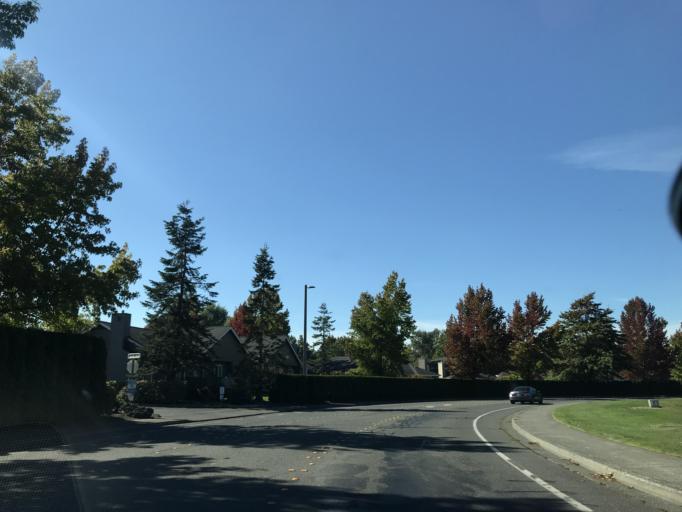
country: US
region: Washington
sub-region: Whatcom County
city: Bellingham
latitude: 48.7946
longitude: -122.4986
